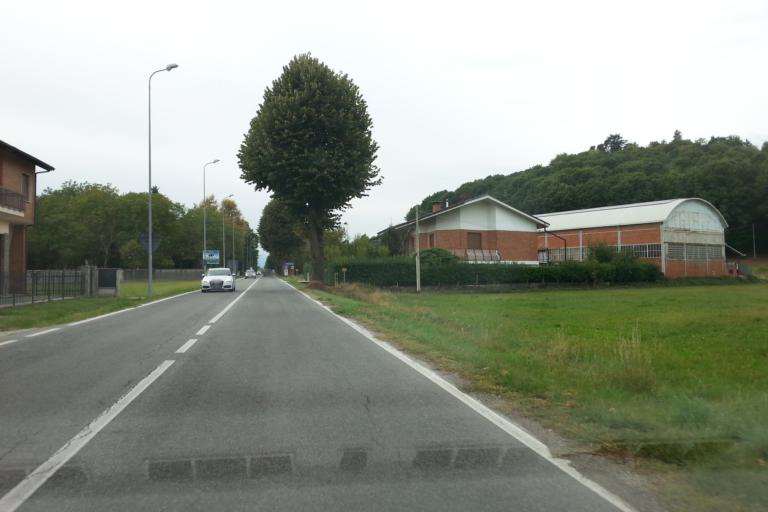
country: IT
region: Piedmont
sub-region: Provincia di Torino
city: Frossasco
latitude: 44.9009
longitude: 7.3580
